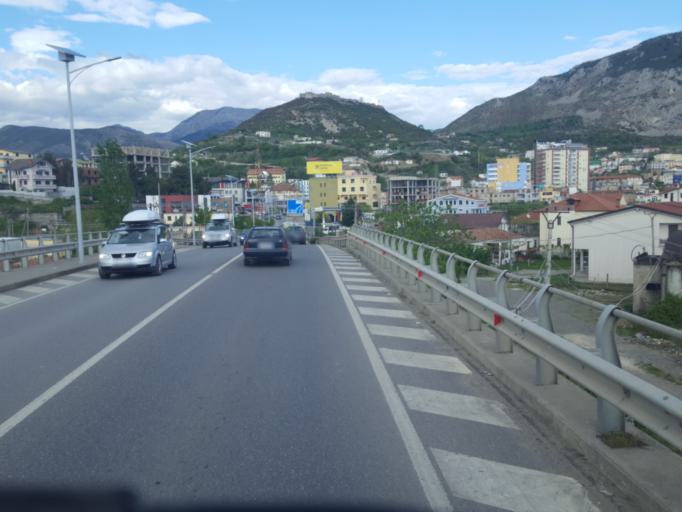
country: AL
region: Lezhe
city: Lezhe
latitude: 41.7790
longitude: 19.6385
